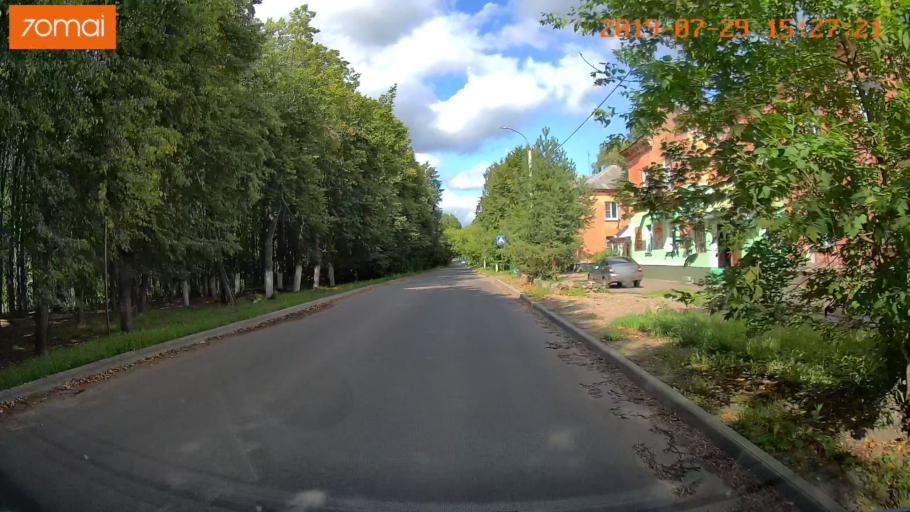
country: RU
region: Ivanovo
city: Bogorodskoye
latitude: 57.0219
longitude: 41.0074
